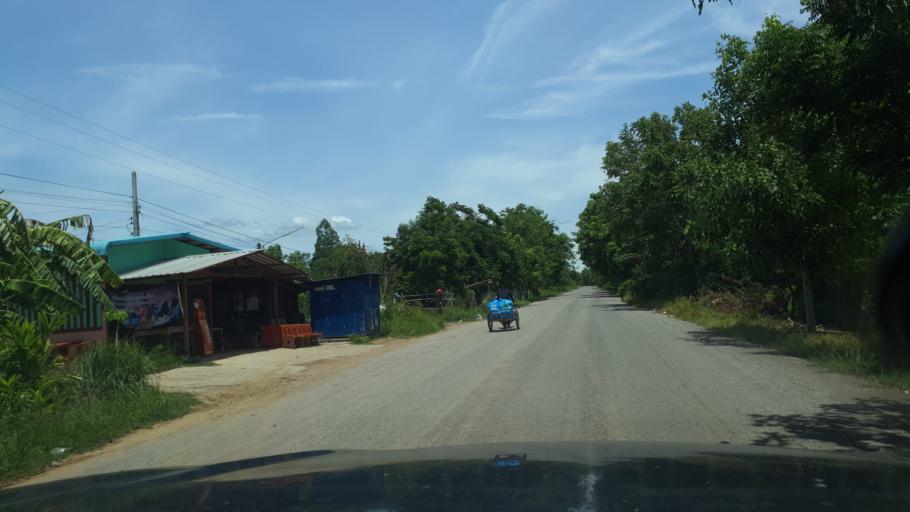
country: TH
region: Sukhothai
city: Ban Na
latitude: 17.0939
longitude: 99.6839
